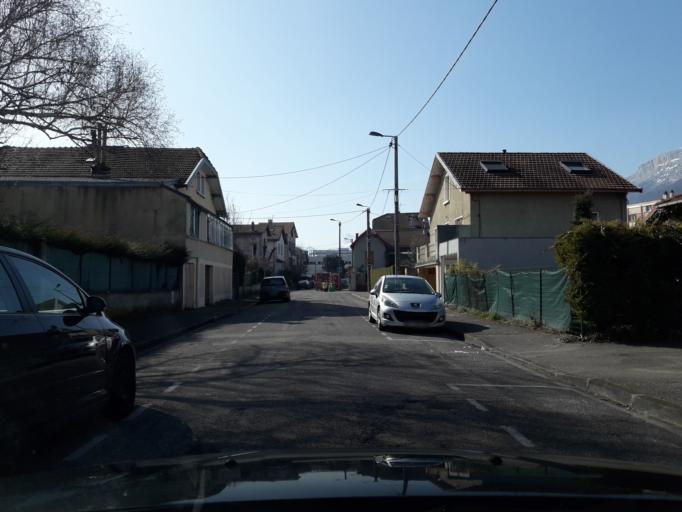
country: FR
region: Rhone-Alpes
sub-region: Departement de l'Isere
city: Grenoble
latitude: 45.1693
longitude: 5.7198
